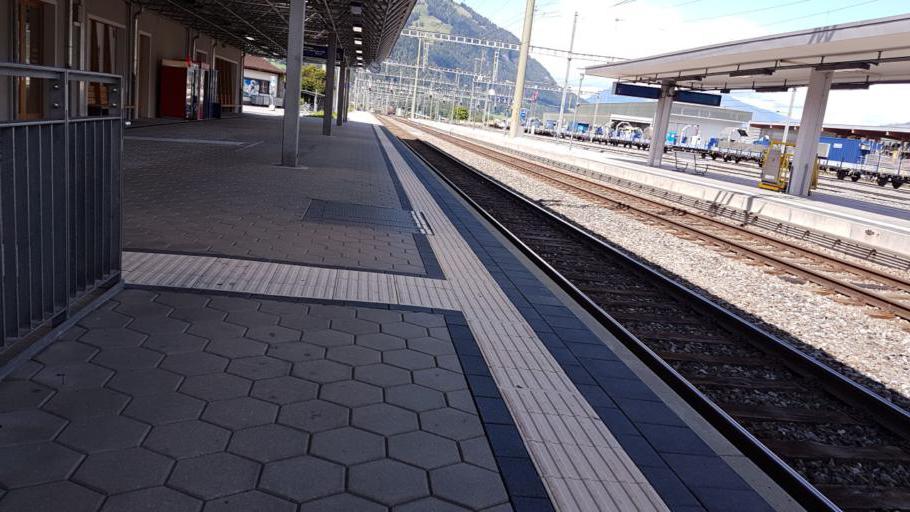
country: CH
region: Bern
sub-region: Frutigen-Niedersimmental District
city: Frutigen
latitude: 46.5887
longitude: 7.6515
